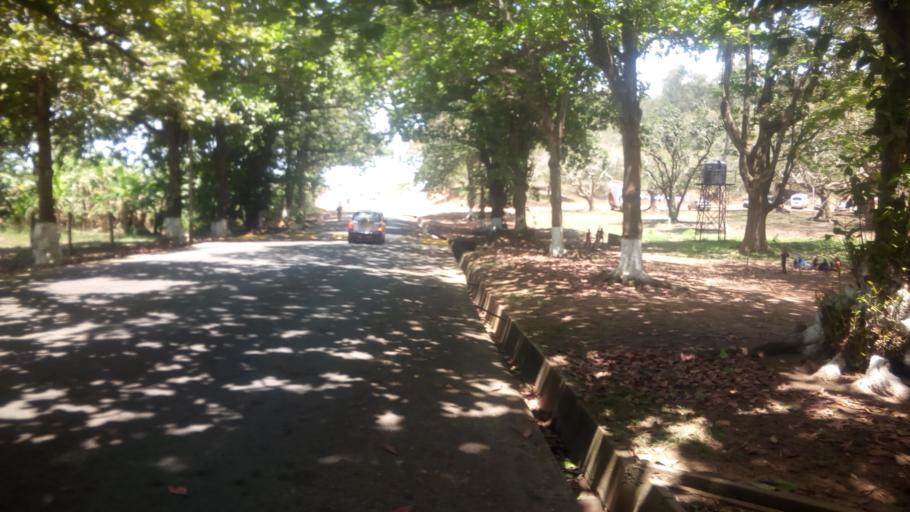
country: GH
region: Central
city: Cape Coast
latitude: 5.1083
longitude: -1.2855
